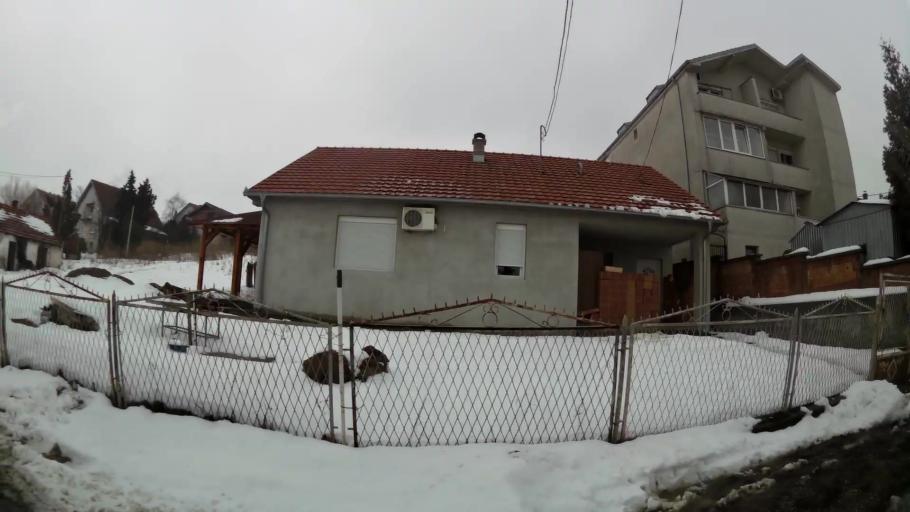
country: RS
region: Central Serbia
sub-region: Belgrade
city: Zvezdara
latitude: 44.7464
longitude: 20.5189
